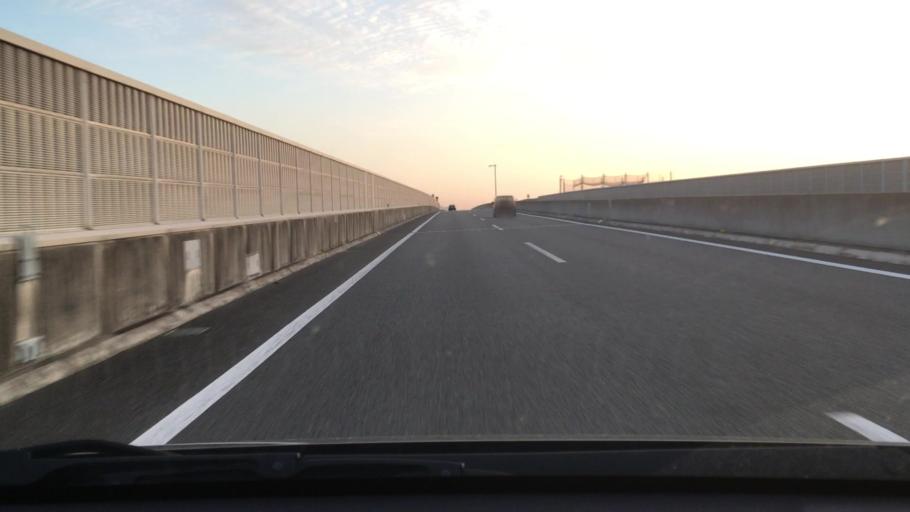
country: JP
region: Fukuoka
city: Maebaru-chuo
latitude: 33.5497
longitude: 130.2159
